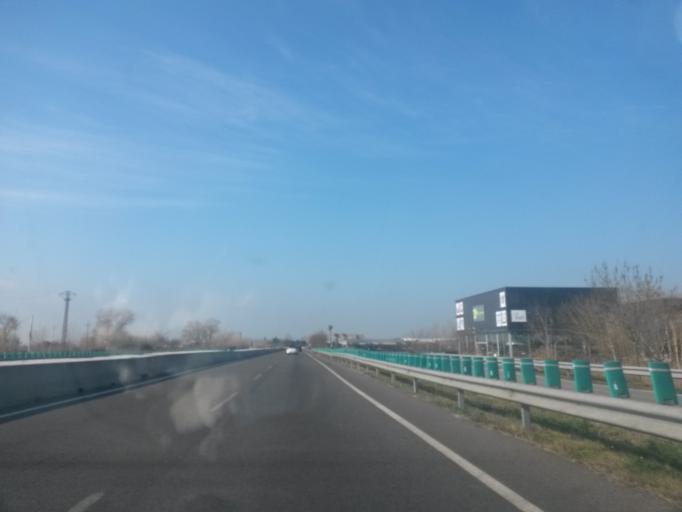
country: ES
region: Catalonia
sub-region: Provincia de Girona
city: Fortia
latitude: 42.2604
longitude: 3.0436
